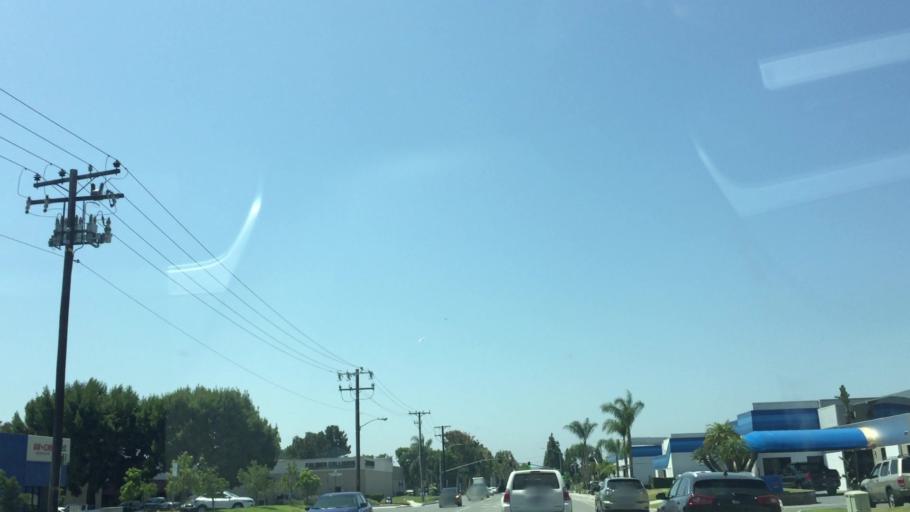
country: US
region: California
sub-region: Orange County
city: Fountain Valley
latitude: 33.7110
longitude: -117.9284
